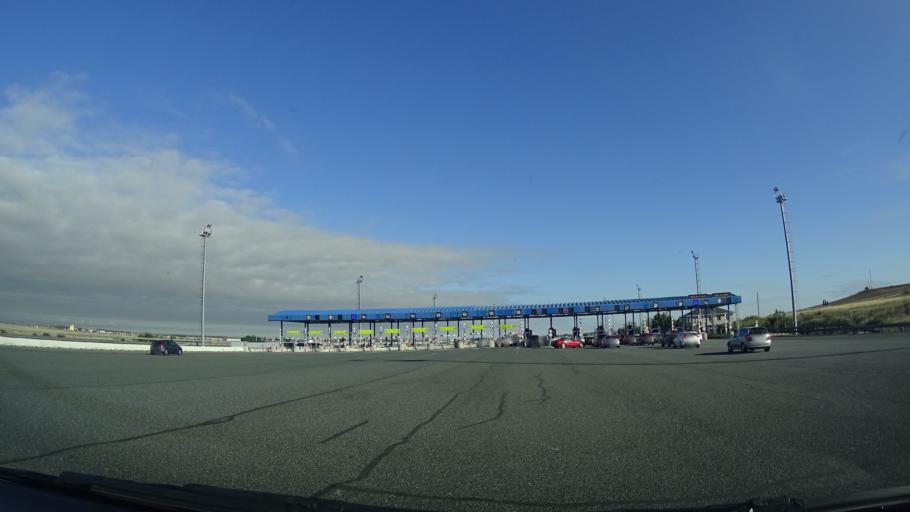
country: ES
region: Castille and Leon
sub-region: Provincia de Avila
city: Sanchidrian
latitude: 40.8833
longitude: -4.5717
